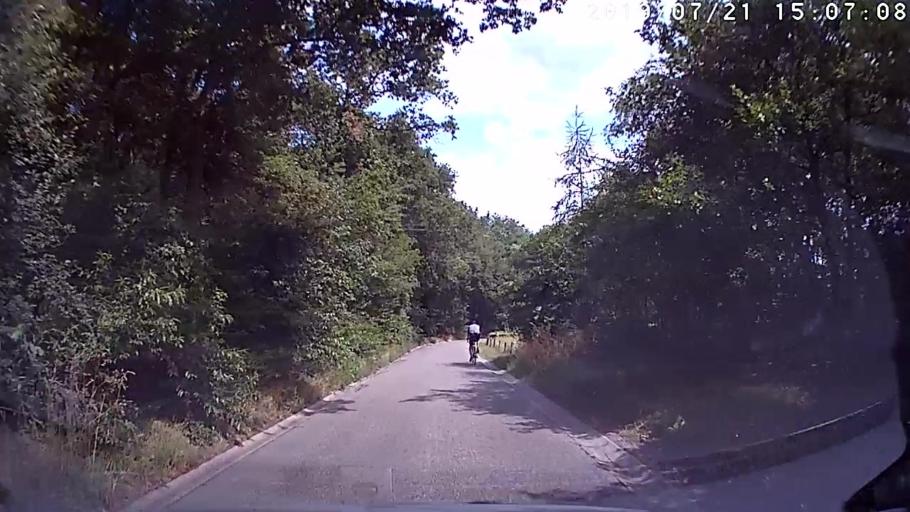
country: NL
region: Overijssel
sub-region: Gemeente Raalte
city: Heino
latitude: 52.4502
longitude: 6.2119
